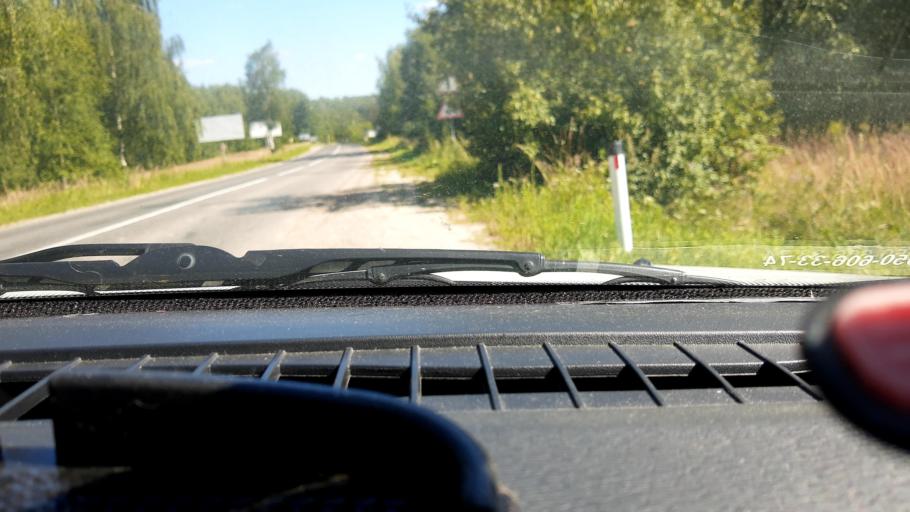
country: RU
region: Nizjnij Novgorod
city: Zavolzh'ye
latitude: 56.6901
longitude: 43.4240
